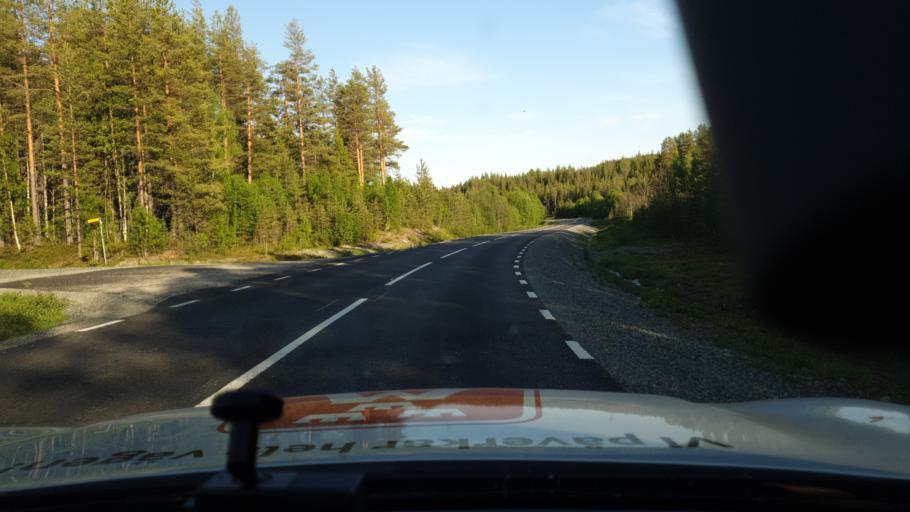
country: SE
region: Vaesterbotten
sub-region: Lycksele Kommun
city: Lycksele
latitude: 64.2776
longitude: 18.6628
